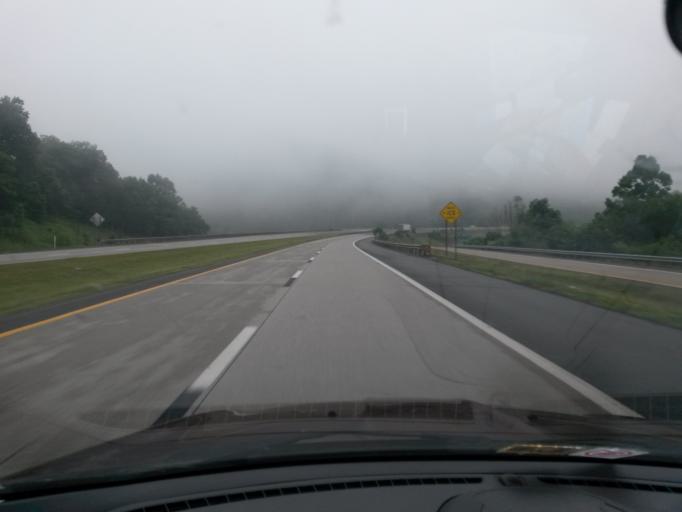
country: US
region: West Virginia
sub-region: Summers County
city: Hinton
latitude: 37.8089
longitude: -80.8153
